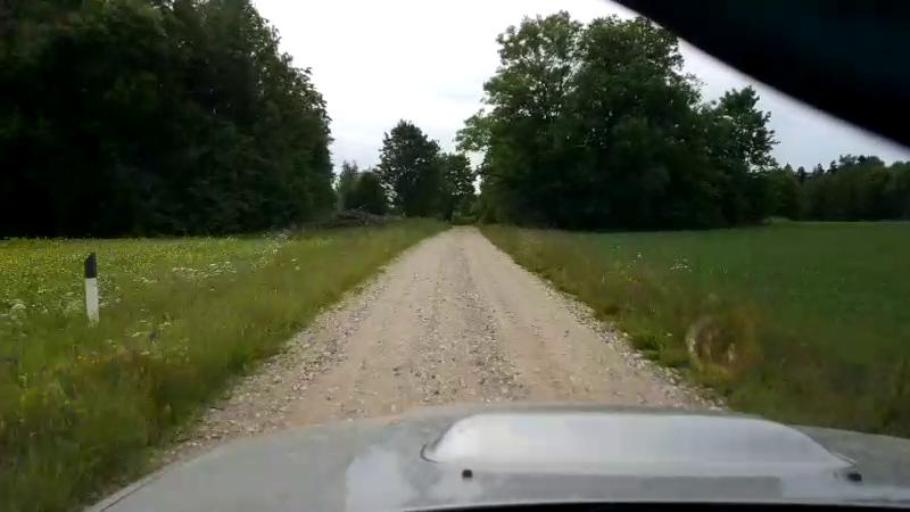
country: EE
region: Paernumaa
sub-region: Tootsi vald
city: Tootsi
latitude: 58.5503
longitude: 24.7442
